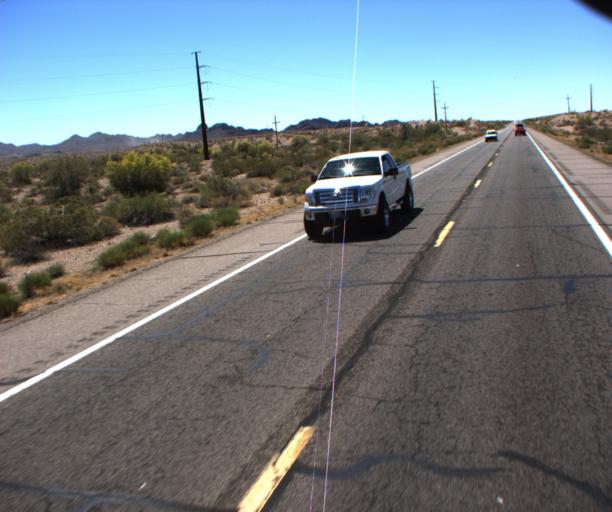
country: US
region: Arizona
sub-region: Mohave County
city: Desert Hills
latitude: 34.6674
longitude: -114.3121
